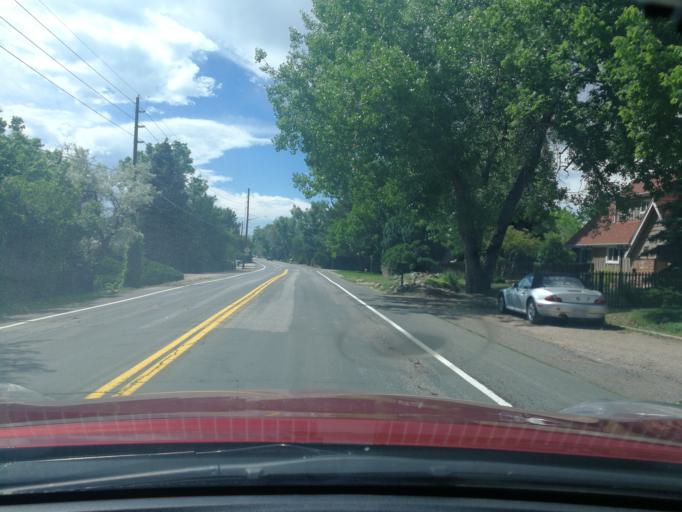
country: US
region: Colorado
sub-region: Arapahoe County
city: Littleton
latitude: 39.5947
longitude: -105.0037
